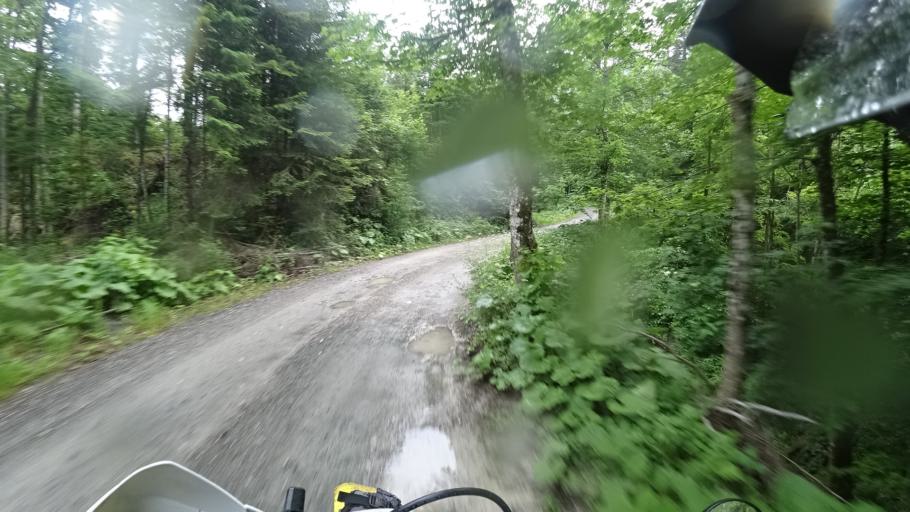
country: HR
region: Primorsko-Goranska
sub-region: Grad Delnice
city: Delnice
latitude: 45.3261
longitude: 14.9287
